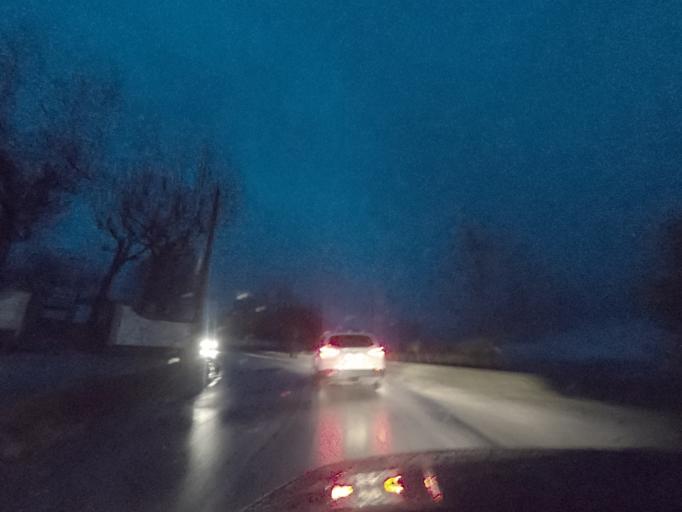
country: PT
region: Vila Real
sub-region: Sabrosa
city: Vilela
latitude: 41.2288
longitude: -7.5646
